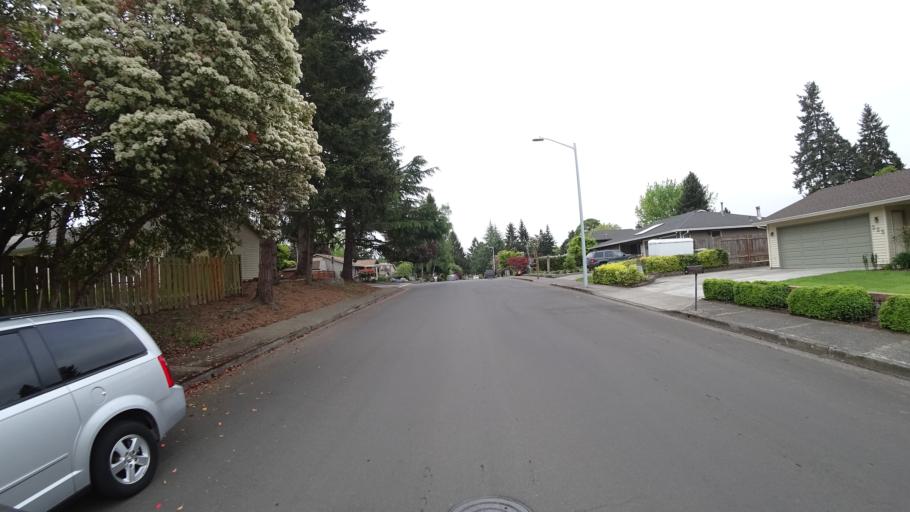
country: US
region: Oregon
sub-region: Washington County
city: Aloha
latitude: 45.5182
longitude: -122.8772
